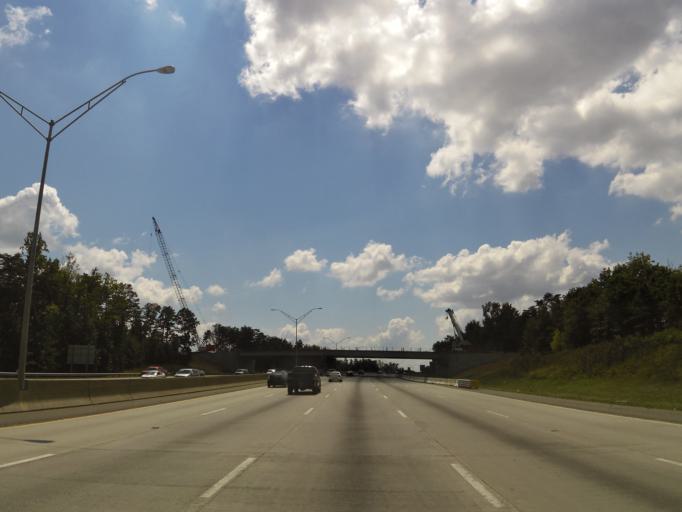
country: US
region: North Carolina
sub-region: Mecklenburg County
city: Charlotte
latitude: 35.2999
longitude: -80.7634
